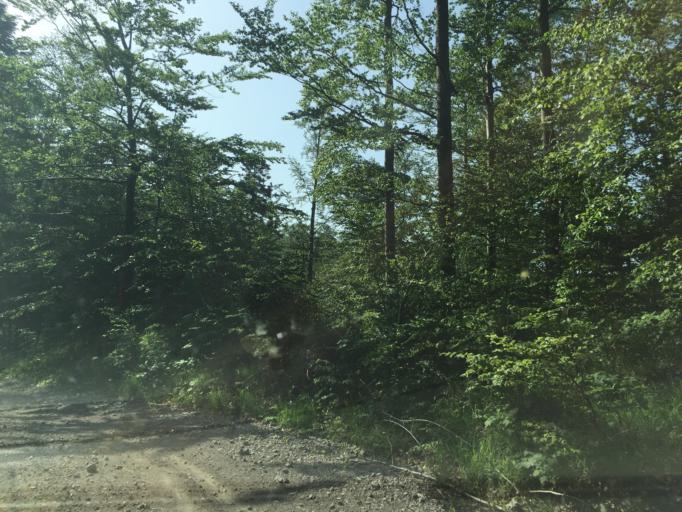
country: HR
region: Primorsko-Goranska
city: Podhum
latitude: 45.4166
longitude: 14.5824
